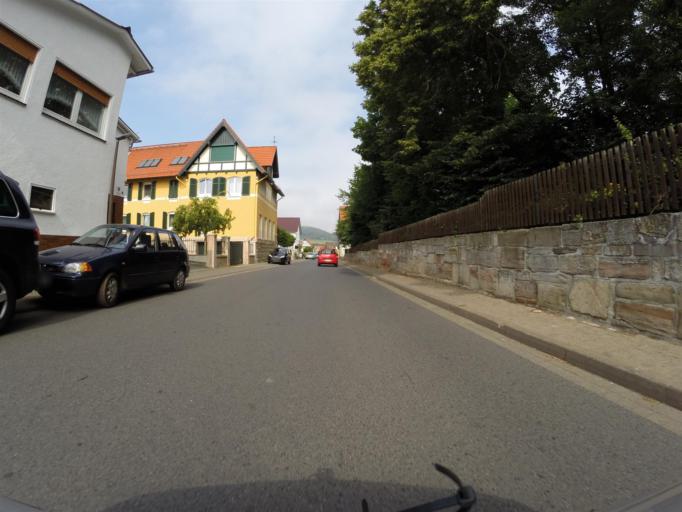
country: DE
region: Hesse
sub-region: Regierungsbezirk Kassel
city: Eschwege
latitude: 51.1491
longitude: 9.9993
